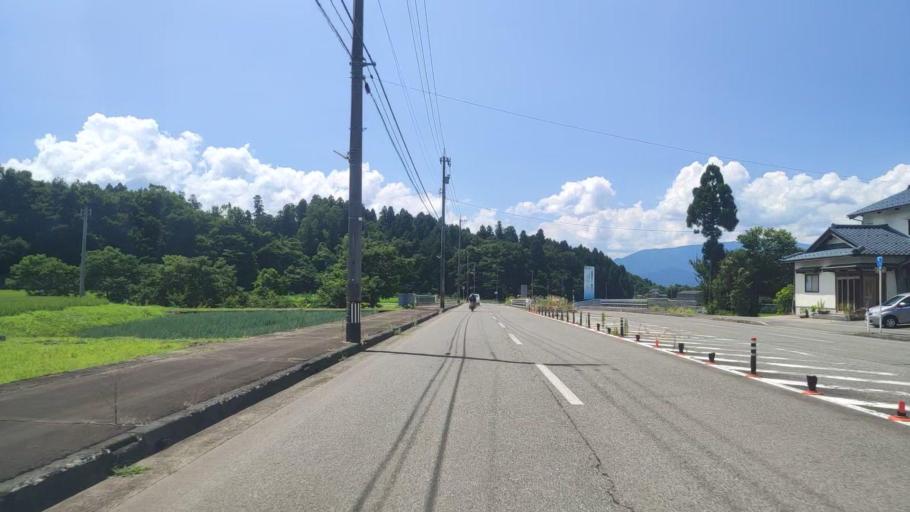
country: JP
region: Fukui
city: Katsuyama
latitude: 36.0330
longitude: 136.5203
